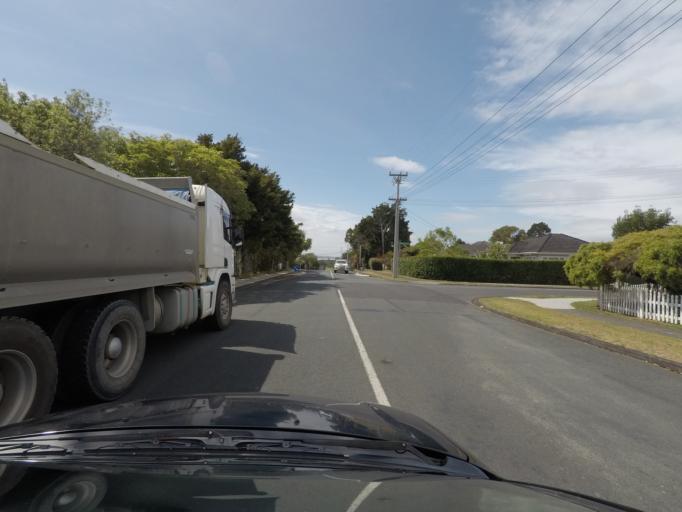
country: NZ
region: Auckland
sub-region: Auckland
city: Waitakere
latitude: -36.8979
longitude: 174.6677
